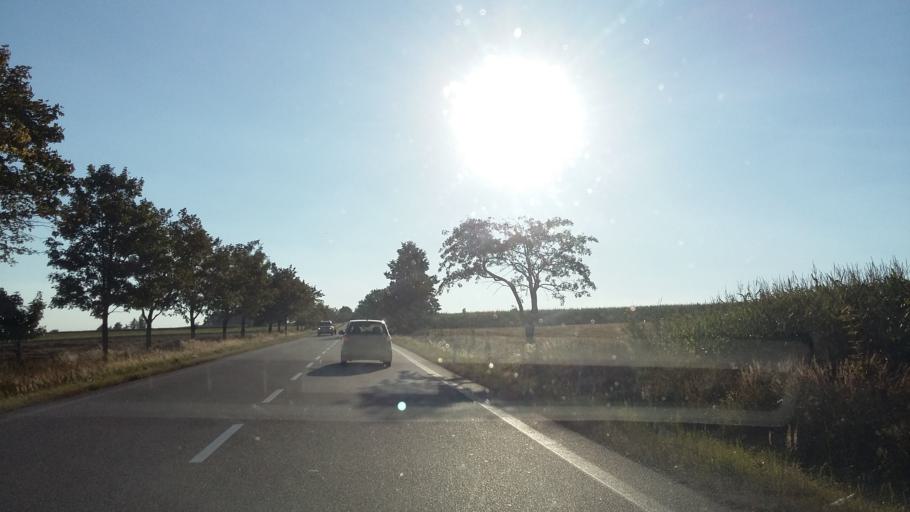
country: CZ
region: Vysocina
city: Kamenice
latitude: 49.3965
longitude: 15.7458
